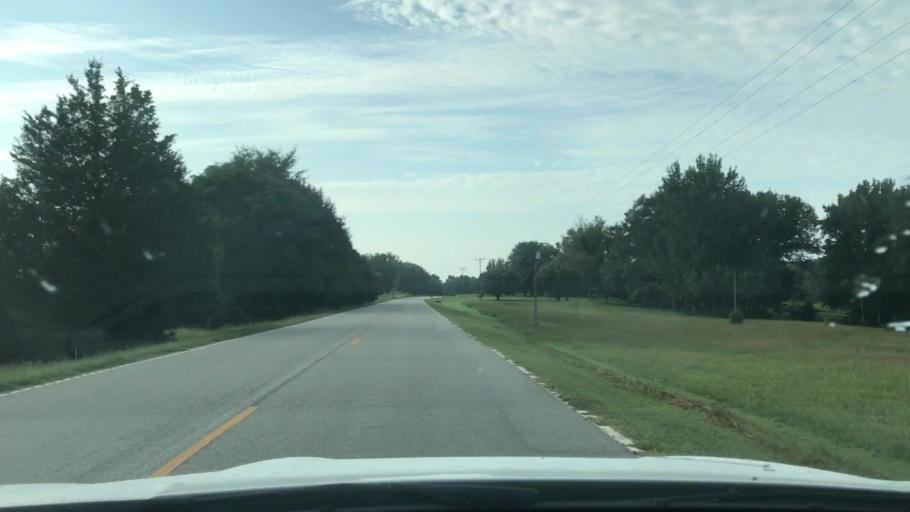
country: US
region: South Carolina
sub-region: Spartanburg County
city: Roebuck
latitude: 34.8326
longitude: -81.9252
